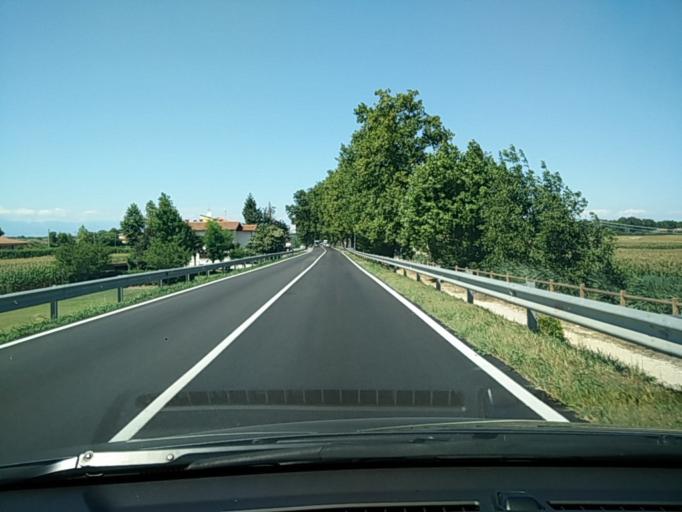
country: IT
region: Veneto
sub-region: Provincia di Venezia
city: La Salute di Livenza
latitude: 45.6910
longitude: 12.8448
